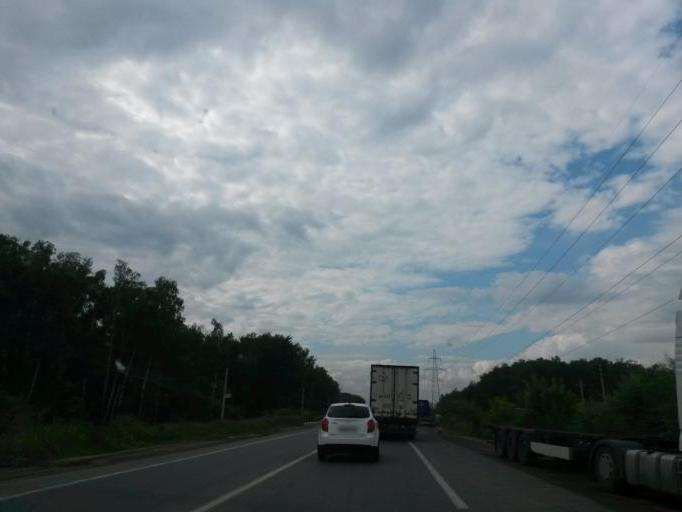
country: RU
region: Moskovskaya
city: Shcherbinka
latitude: 55.4900
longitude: 37.5933
